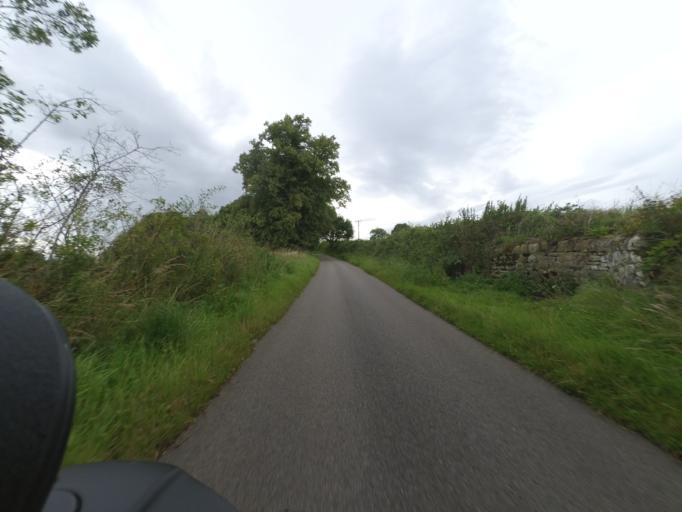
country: GB
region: Scotland
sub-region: Highland
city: Conon Bridge
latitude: 57.5138
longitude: -4.3699
